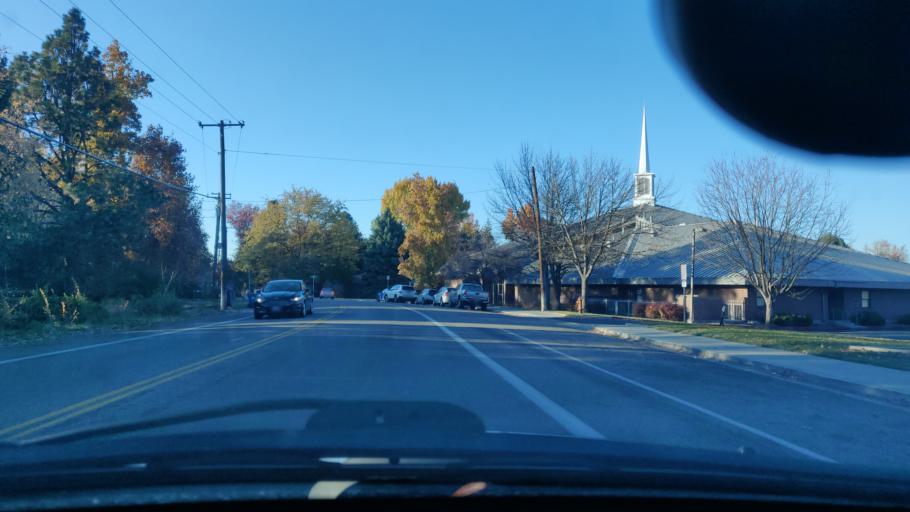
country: US
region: Idaho
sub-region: Ada County
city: Boise
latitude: 43.6001
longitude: -116.2072
